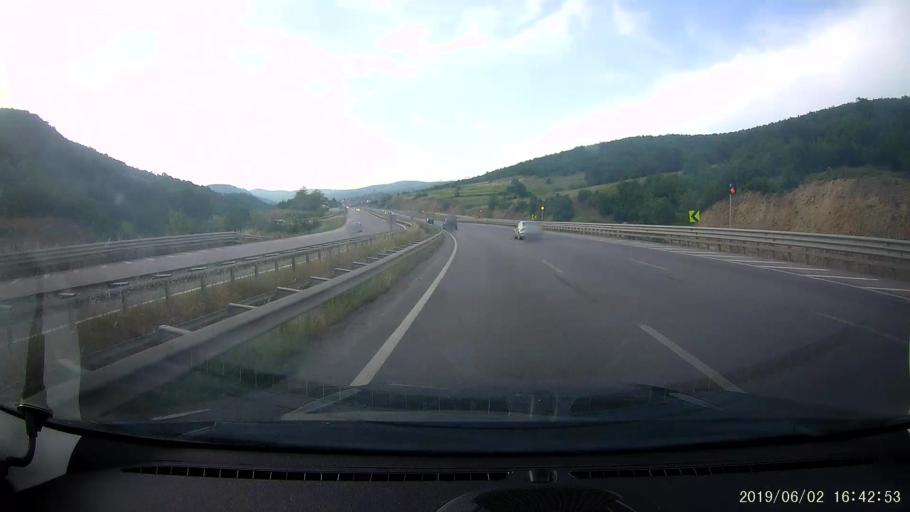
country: TR
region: Samsun
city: Kavak
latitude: 41.1256
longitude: 36.1379
